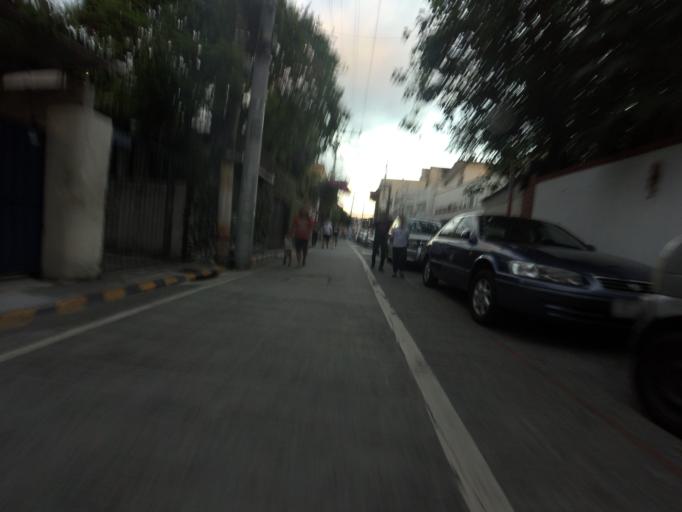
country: PH
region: Metro Manila
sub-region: San Juan
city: San Juan
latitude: 14.5818
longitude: 121.0151
